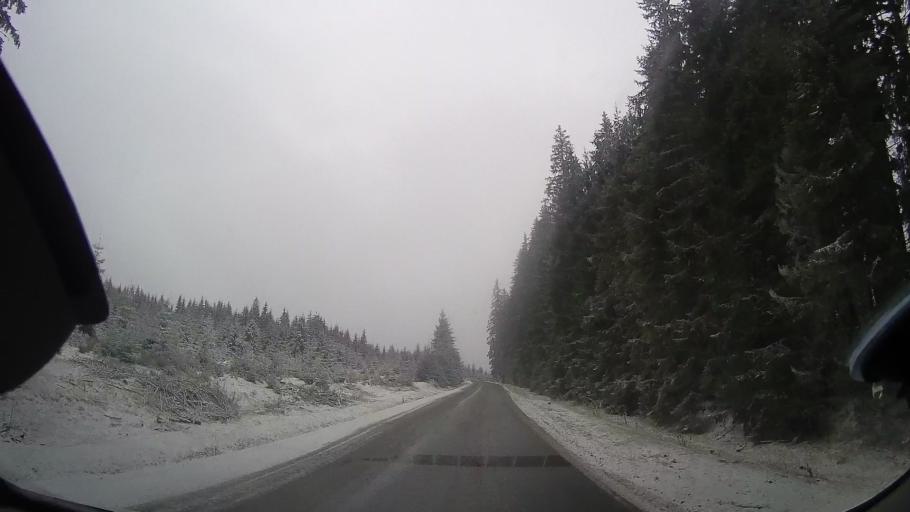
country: RO
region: Cluj
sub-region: Comuna Belis
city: Belis
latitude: 46.6417
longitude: 23.0580
